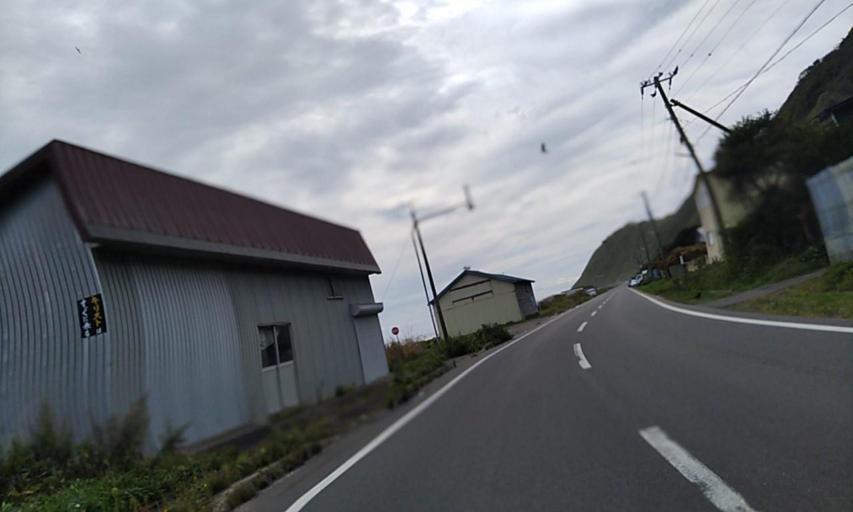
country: JP
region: Hokkaido
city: Kushiro
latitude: 42.7976
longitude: 143.8089
